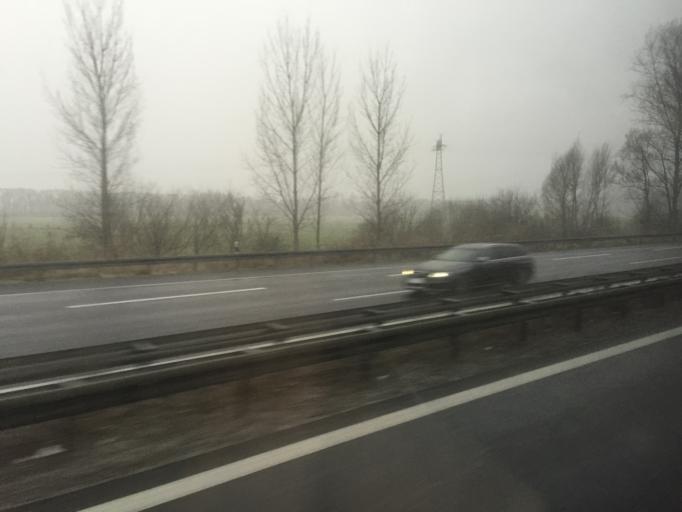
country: DE
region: Brandenburg
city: Velten
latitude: 52.7059
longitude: 13.1823
